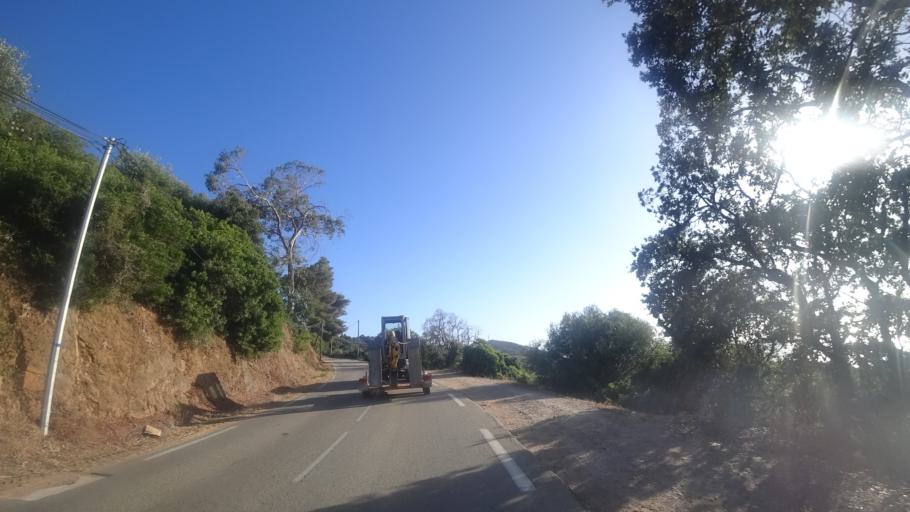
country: FR
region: Corsica
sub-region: Departement de la Corse-du-Sud
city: Cargese
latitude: 42.1424
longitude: 8.6020
